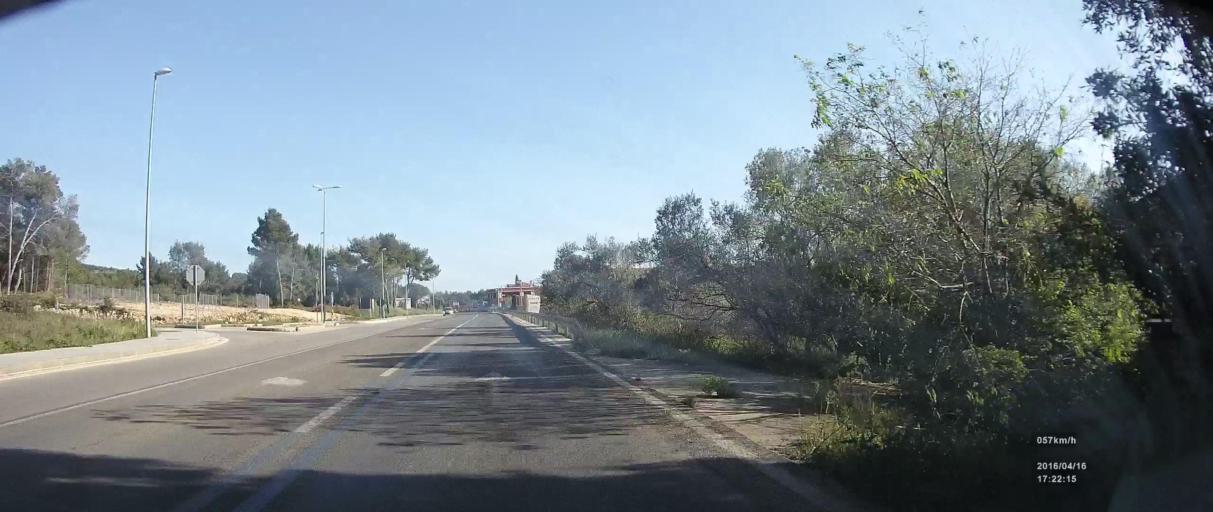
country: HR
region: Zadarska
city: Bibinje
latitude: 44.0847
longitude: 15.2838
